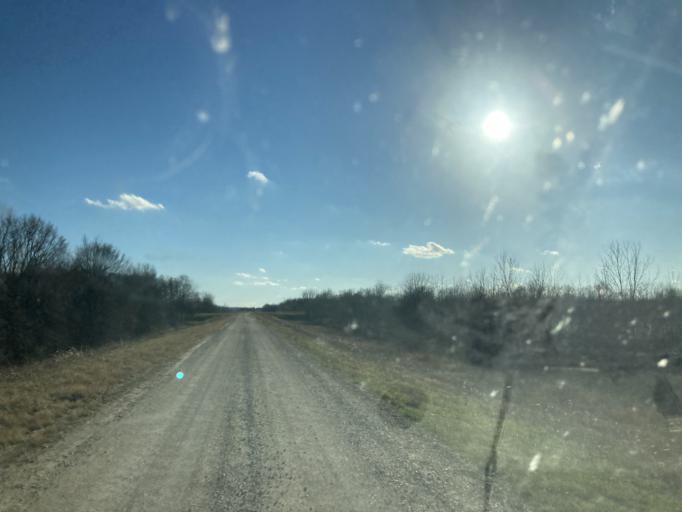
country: US
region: Mississippi
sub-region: Yazoo County
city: Yazoo City
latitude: 32.9193
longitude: -90.5535
